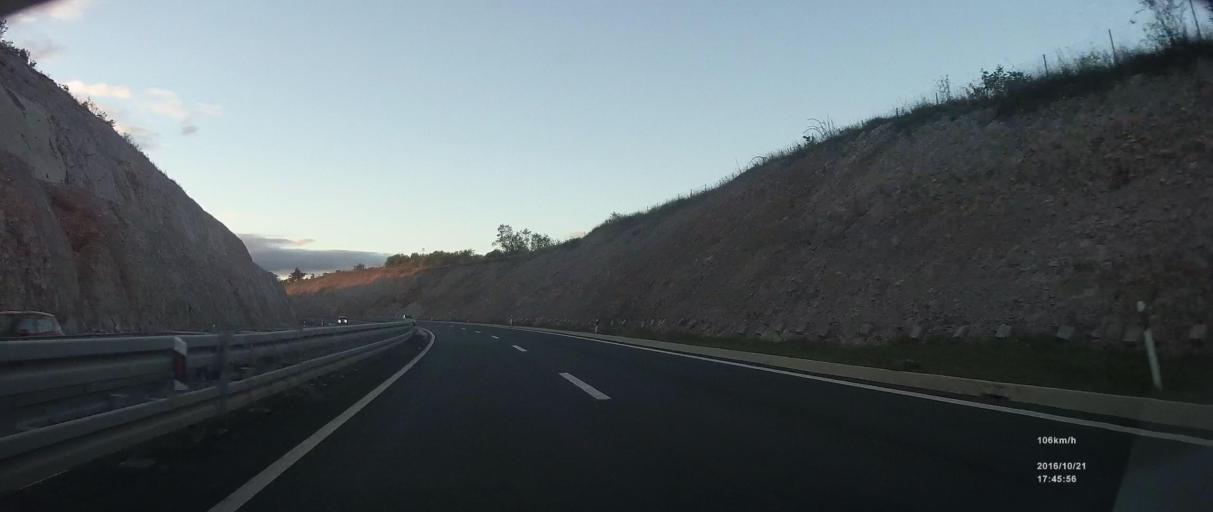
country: HR
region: Primorsko-Goranska
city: Krasica
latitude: 45.2964
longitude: 14.5703
